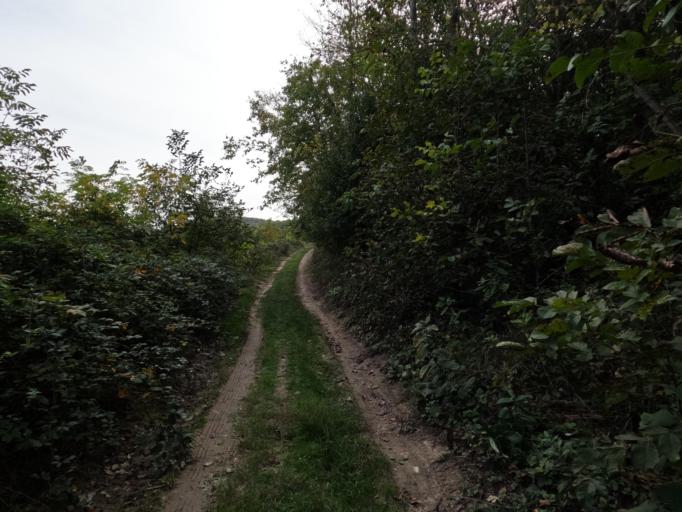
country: HU
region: Tolna
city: Szentgalpuszta
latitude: 46.3386
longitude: 18.6483
